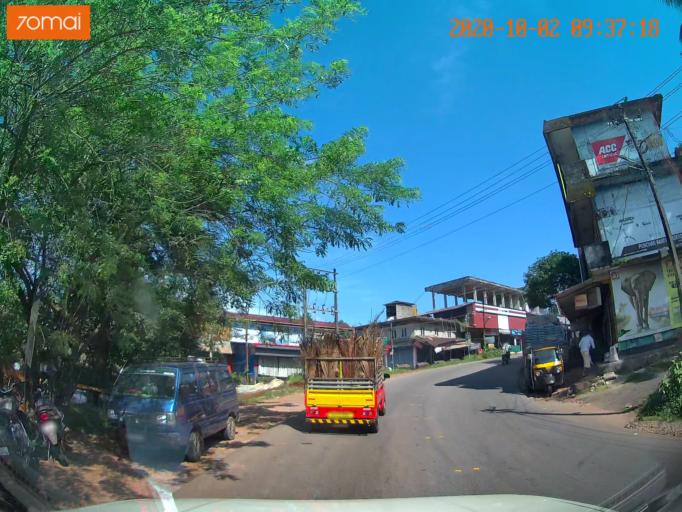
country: IN
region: Kerala
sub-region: Kozhikode
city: Nadapuram
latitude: 11.6514
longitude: 75.7537
